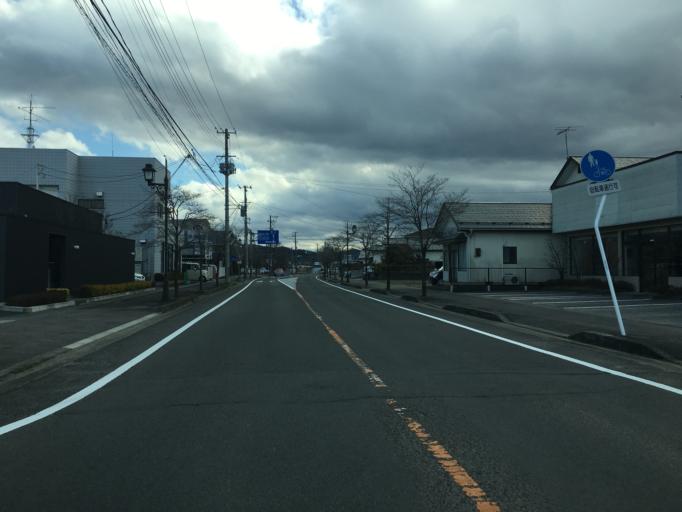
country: JP
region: Fukushima
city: Yanagawamachi-saiwaicho
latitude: 37.8482
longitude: 140.6006
